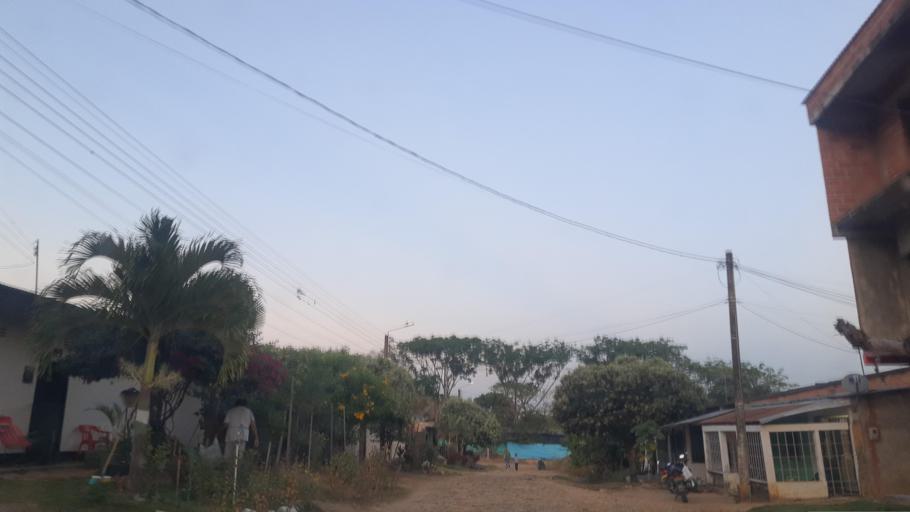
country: CO
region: Arauca
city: Tame
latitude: 6.4566
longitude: -71.7297
